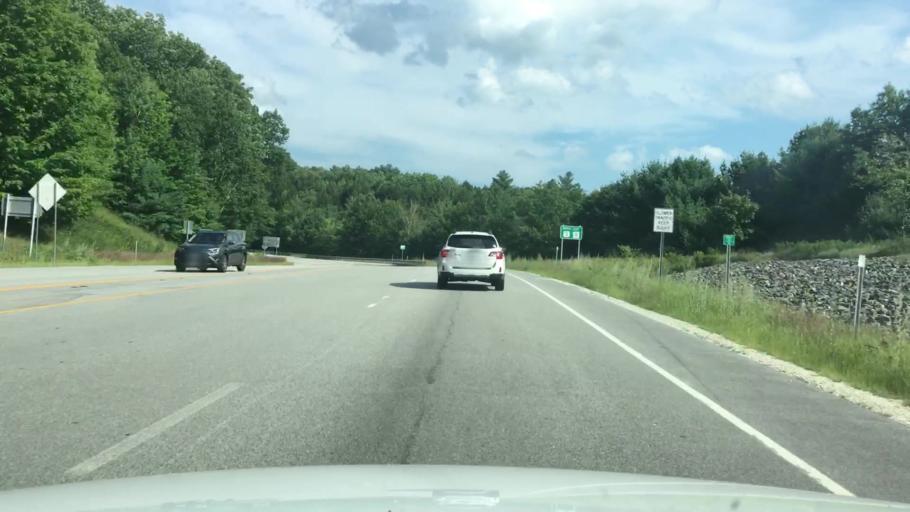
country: US
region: New Hampshire
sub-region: Belknap County
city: Laconia
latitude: 43.5158
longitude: -71.4866
